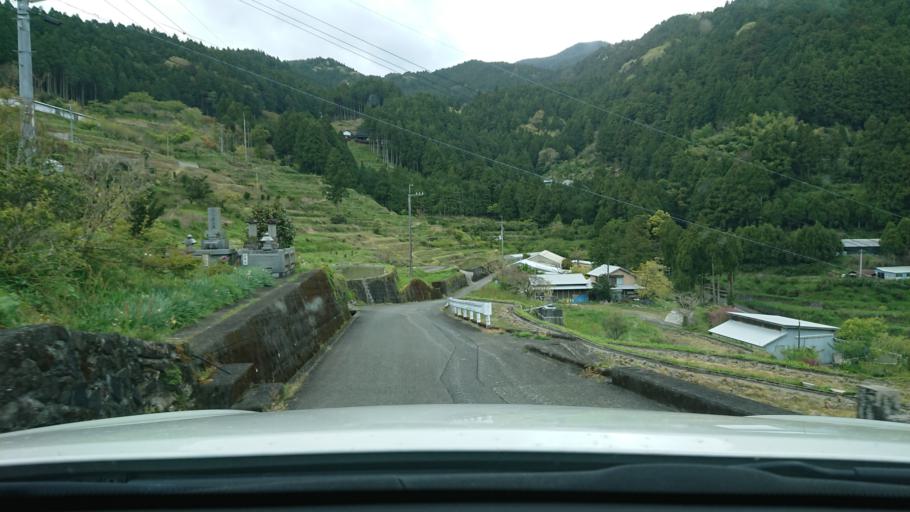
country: JP
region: Tokushima
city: Kamojimacho-jogejima
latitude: 33.8863
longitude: 134.3933
